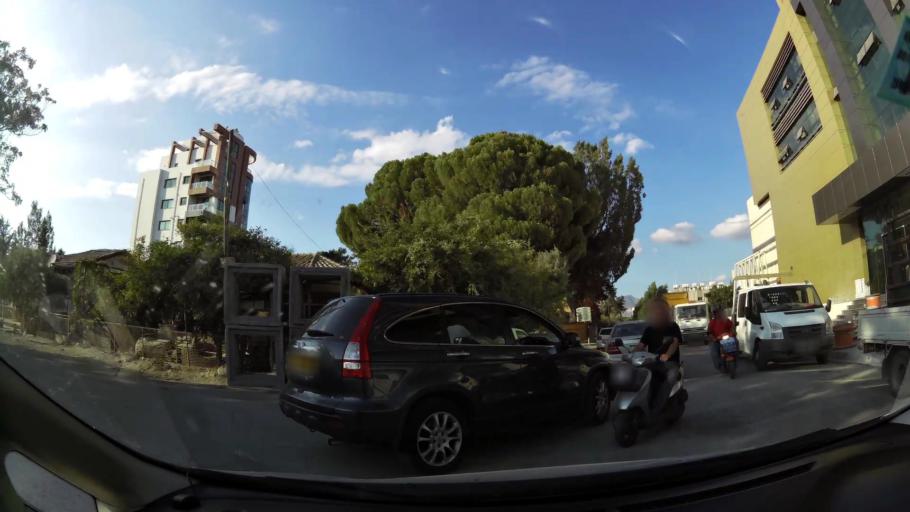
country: CY
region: Lefkosia
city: Nicosia
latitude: 35.1864
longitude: 33.3620
